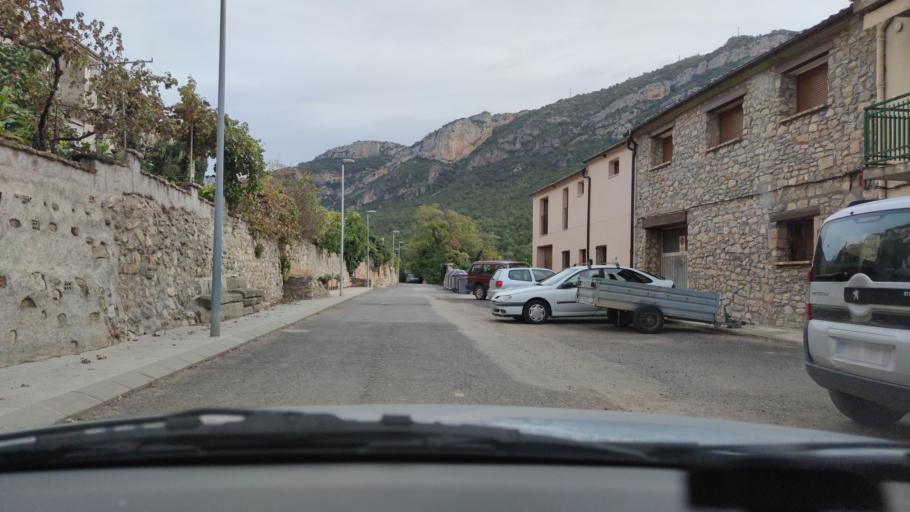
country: ES
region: Catalonia
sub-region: Provincia de Lleida
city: Artesa de Segre
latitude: 41.9945
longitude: 1.0236
